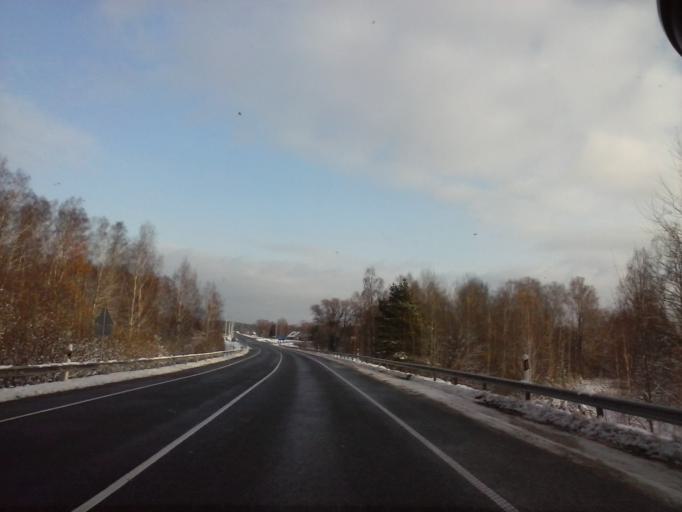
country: EE
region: Tartu
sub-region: Tartu linn
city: Tartu
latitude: 58.3562
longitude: 26.9039
